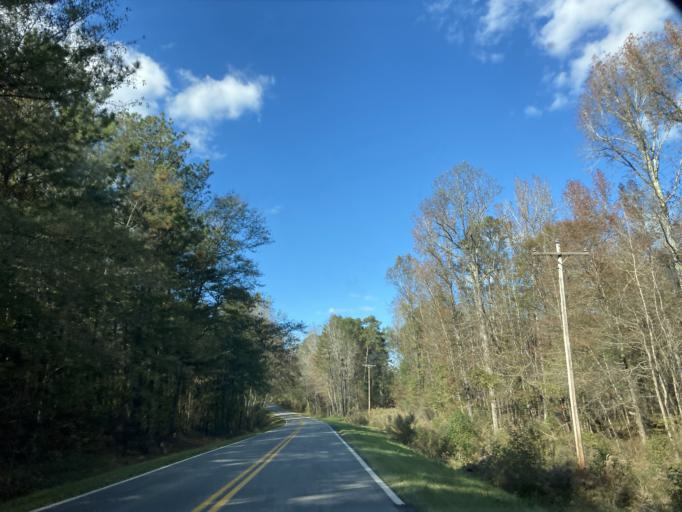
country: US
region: Georgia
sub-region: Jones County
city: Gray
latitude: 32.9439
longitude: -83.5134
